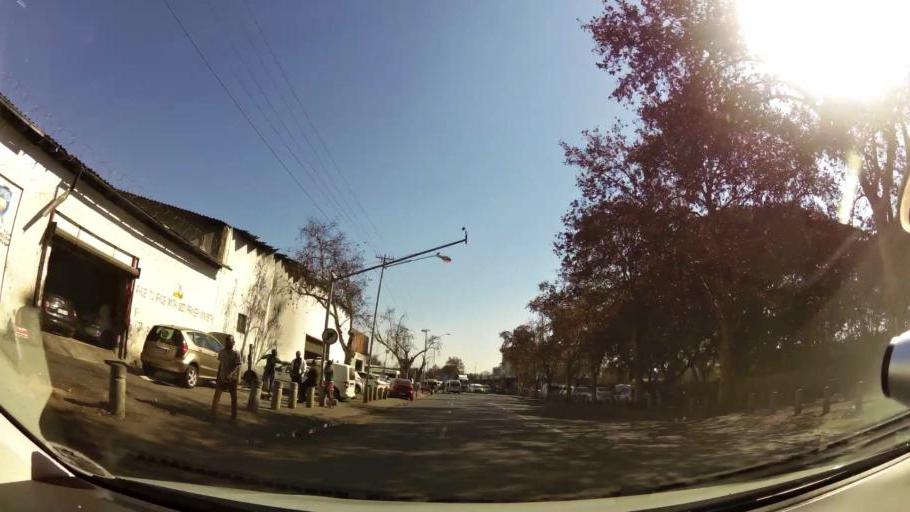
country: ZA
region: Gauteng
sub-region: City of Tshwane Metropolitan Municipality
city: Pretoria
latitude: -25.7405
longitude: 28.1958
